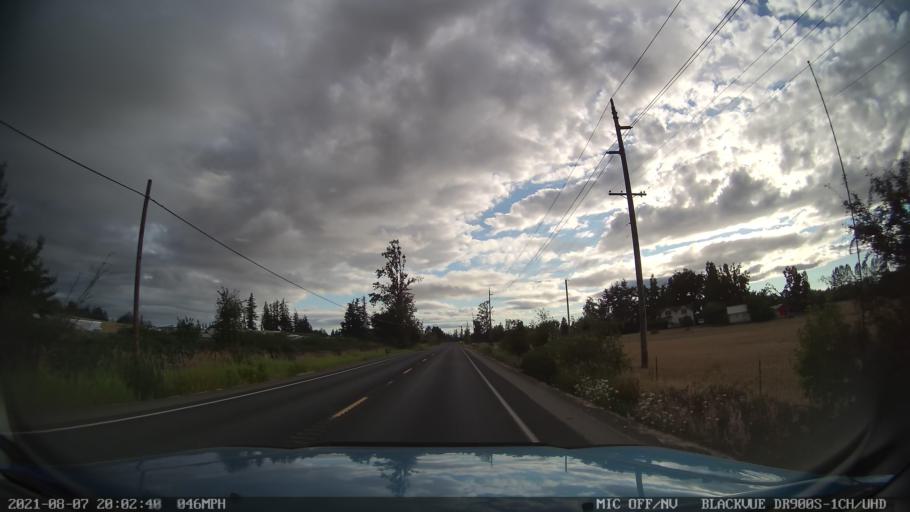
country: US
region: Oregon
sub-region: Marion County
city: Silverton
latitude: 45.0014
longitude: -122.8069
